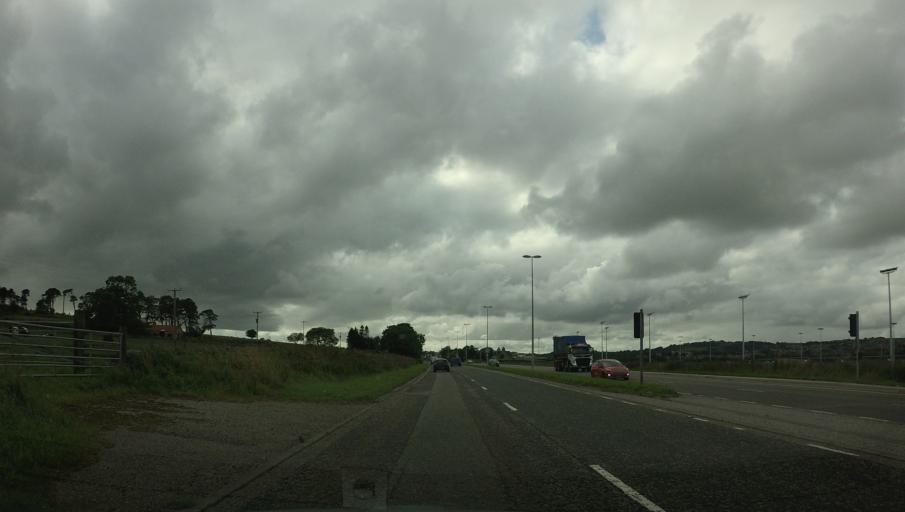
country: GB
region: Scotland
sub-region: Aberdeenshire
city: Westhill
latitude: 57.1471
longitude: -2.2542
